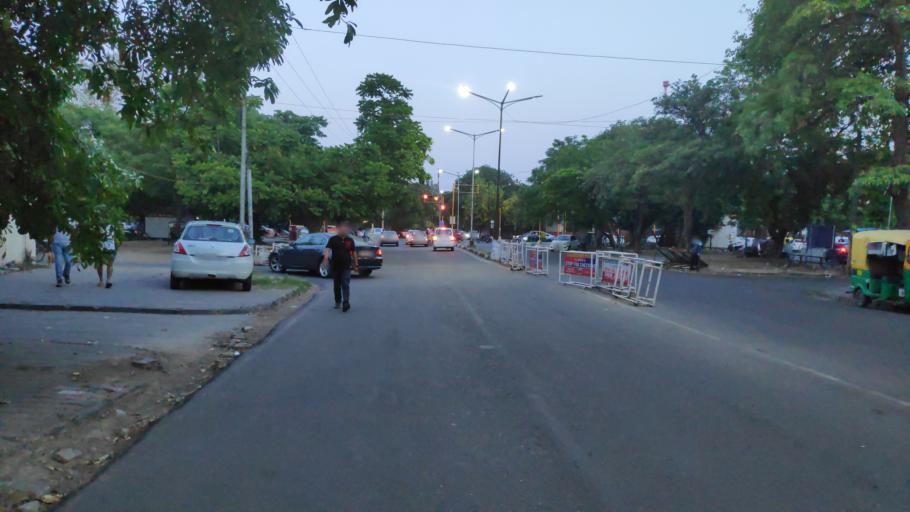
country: IN
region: Chandigarh
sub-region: Chandigarh
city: Chandigarh
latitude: 30.7235
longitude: 76.7623
